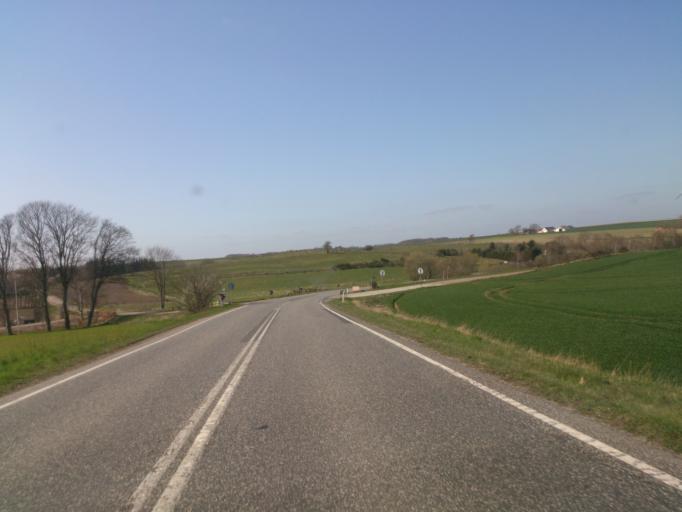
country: DK
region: Central Jutland
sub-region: Viborg Kommune
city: Bjerringbro
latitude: 56.4181
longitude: 9.6718
